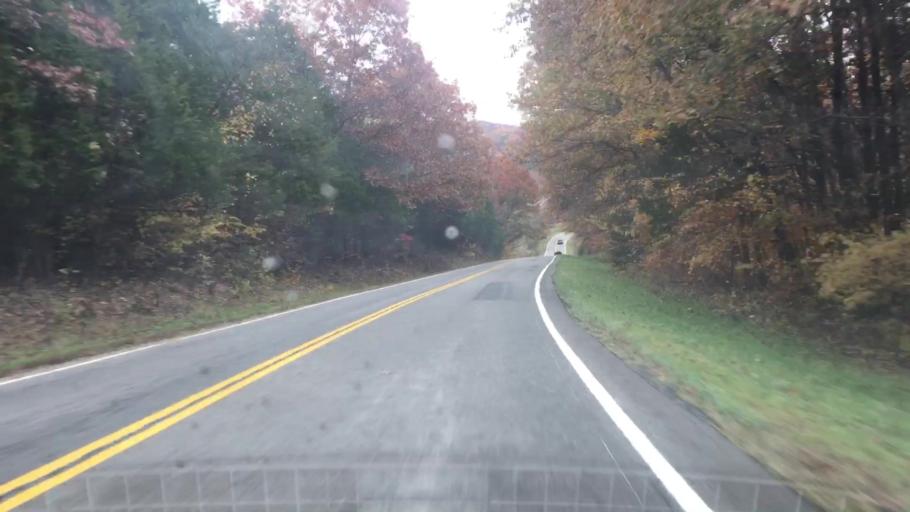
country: US
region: Missouri
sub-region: Gasconade County
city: Hermann
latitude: 38.7089
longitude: -91.6288
